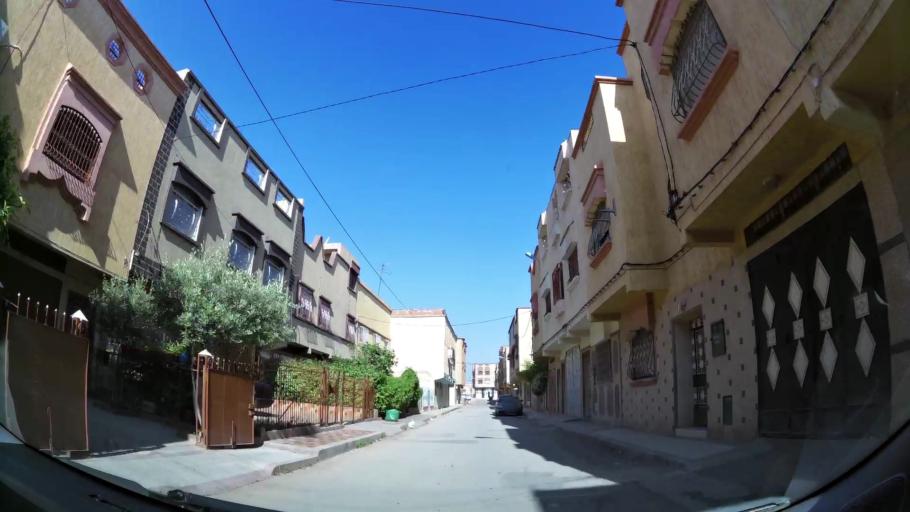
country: MA
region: Oriental
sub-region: Oujda-Angad
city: Oujda
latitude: 34.6831
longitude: -1.9370
